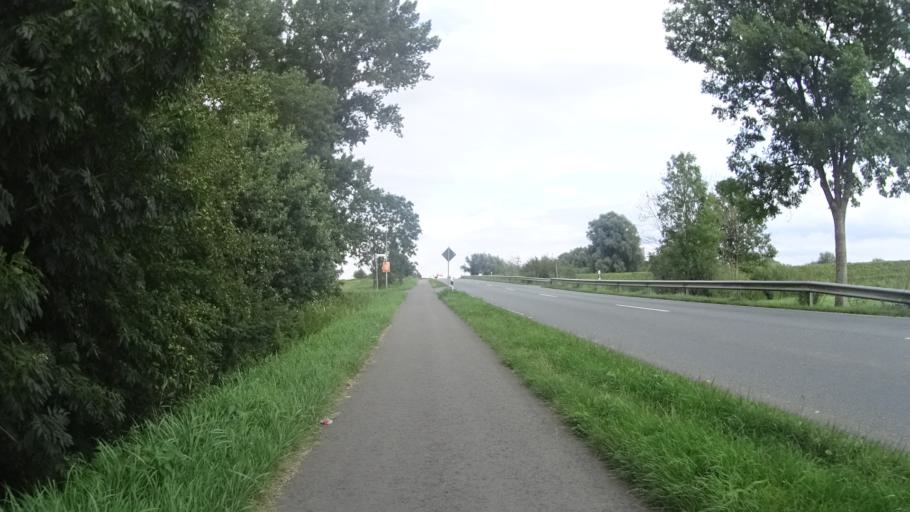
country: DE
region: Lower Saxony
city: Wischhafen
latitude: 53.7850
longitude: 9.3329
